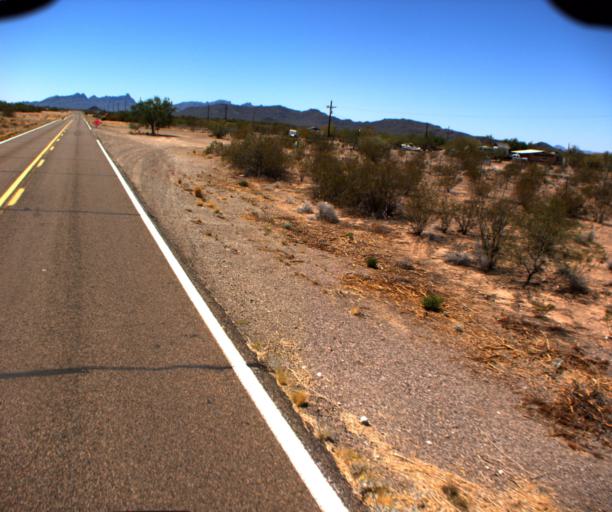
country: US
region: Arizona
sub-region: Pima County
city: Ajo
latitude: 32.2631
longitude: -112.7364
